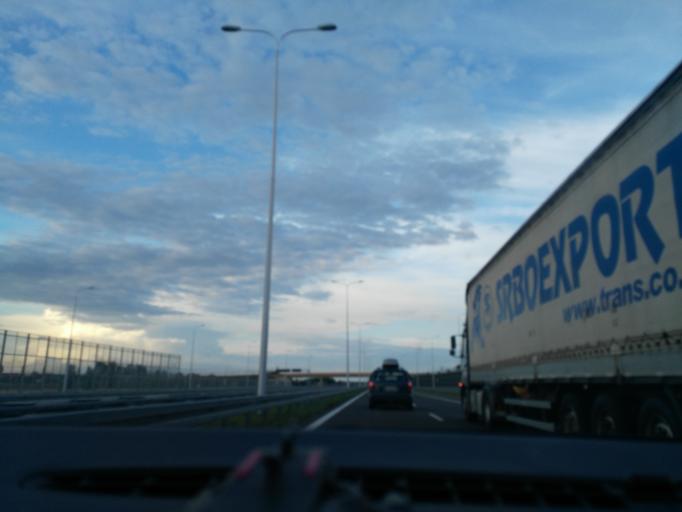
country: PL
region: Lublin Voivodeship
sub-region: Powiat lubelski
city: Jastkow
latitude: 51.2868
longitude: 22.4571
